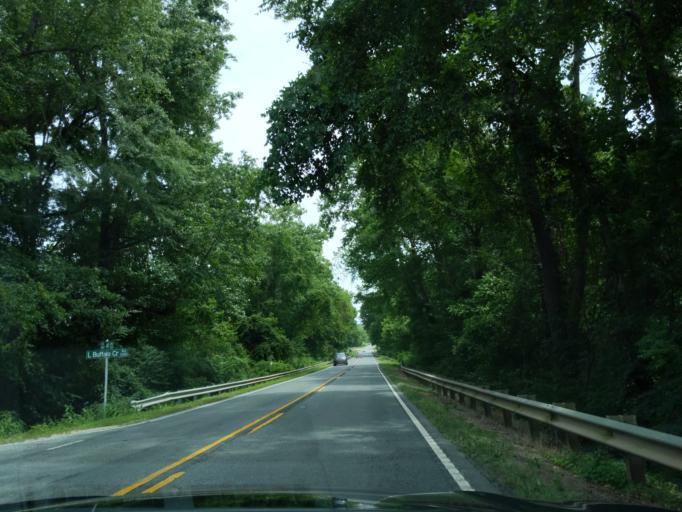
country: US
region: North Carolina
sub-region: Cabarrus County
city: Mount Pleasant
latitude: 35.4330
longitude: -80.4006
